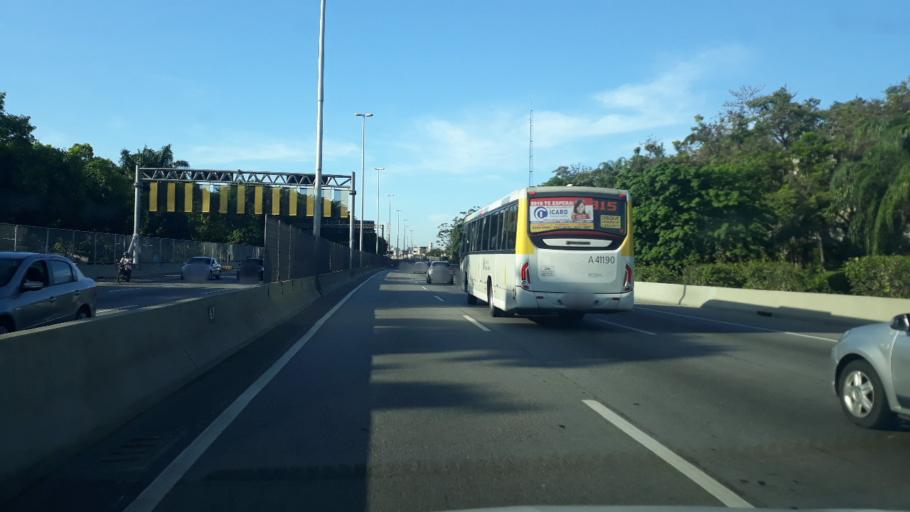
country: BR
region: Rio de Janeiro
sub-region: Sao Joao De Meriti
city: Sao Joao de Meriti
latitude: -22.9461
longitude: -43.3545
